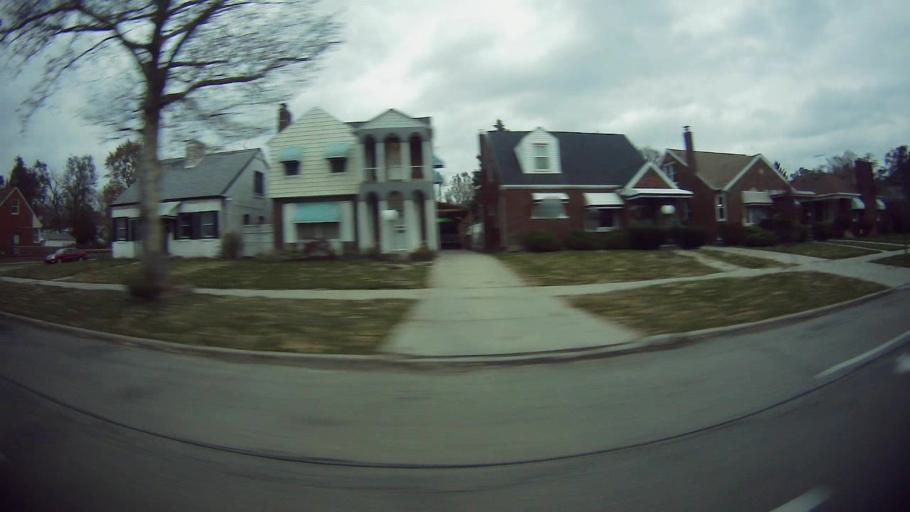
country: US
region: Michigan
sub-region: Macomb County
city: Warren
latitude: 42.4303
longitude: -83.0142
